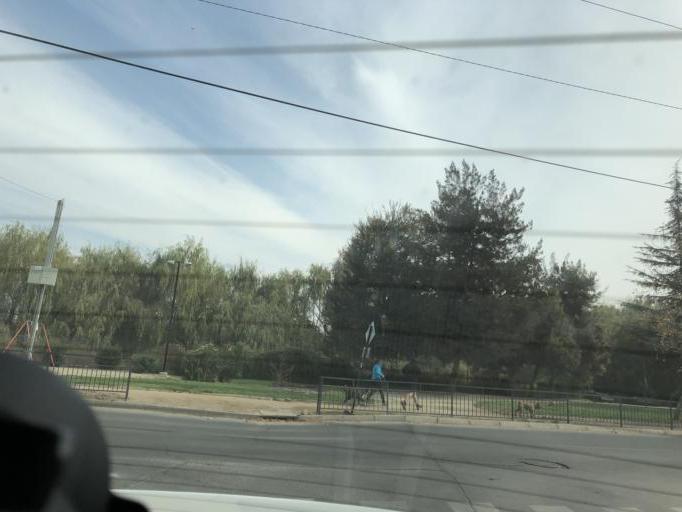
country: CL
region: Santiago Metropolitan
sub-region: Provincia de Cordillera
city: Puente Alto
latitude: -33.5566
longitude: -70.5527
